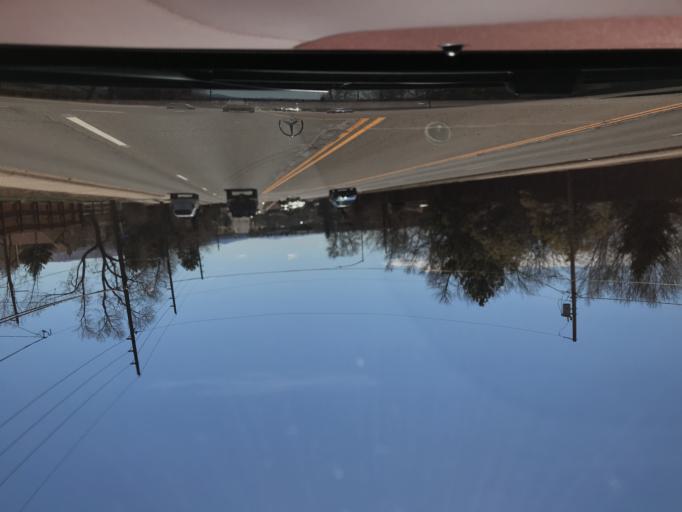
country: US
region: Colorado
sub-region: Jefferson County
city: Arvada
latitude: 39.8065
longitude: -105.1380
